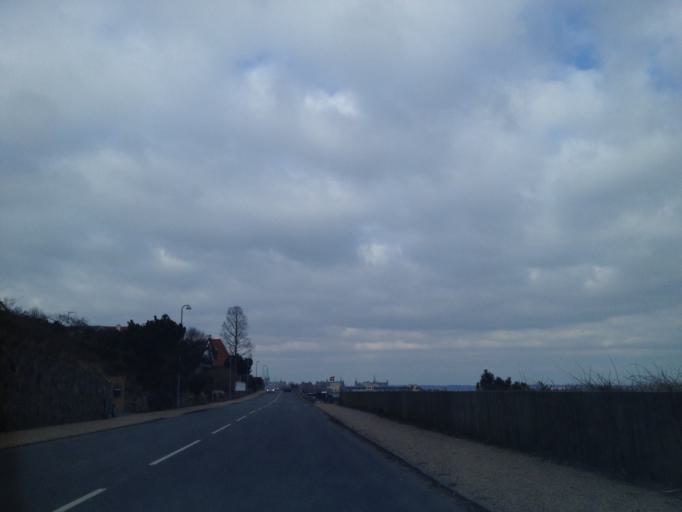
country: DK
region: Capital Region
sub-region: Helsingor Kommune
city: Helsingor
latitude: 56.0224
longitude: 12.6045
